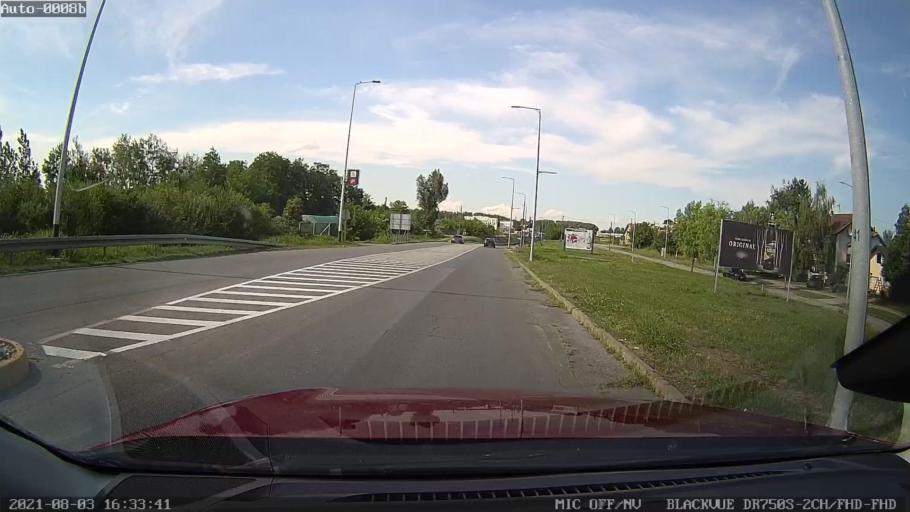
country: HR
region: Osjecko-Baranjska
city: Visnjevac
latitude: 45.5565
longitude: 18.6346
